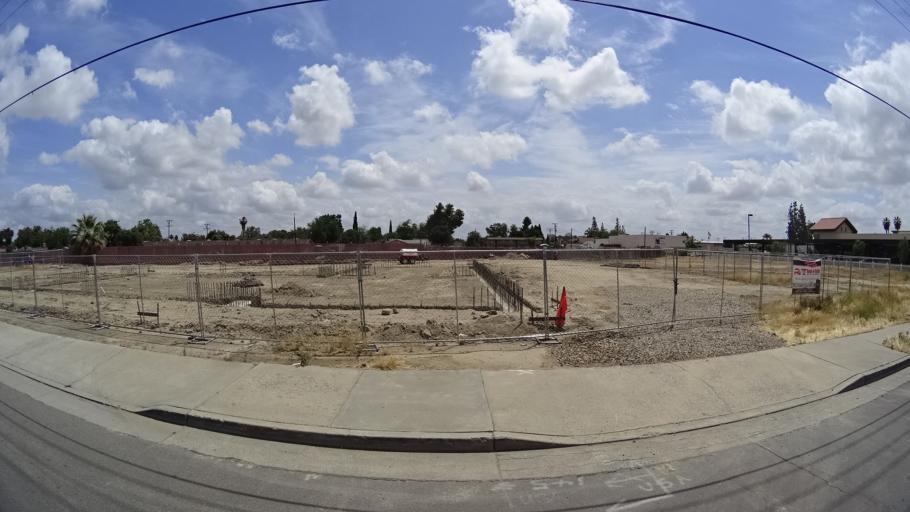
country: US
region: California
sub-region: Kings County
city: Hanford
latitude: 36.3298
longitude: -119.6551
